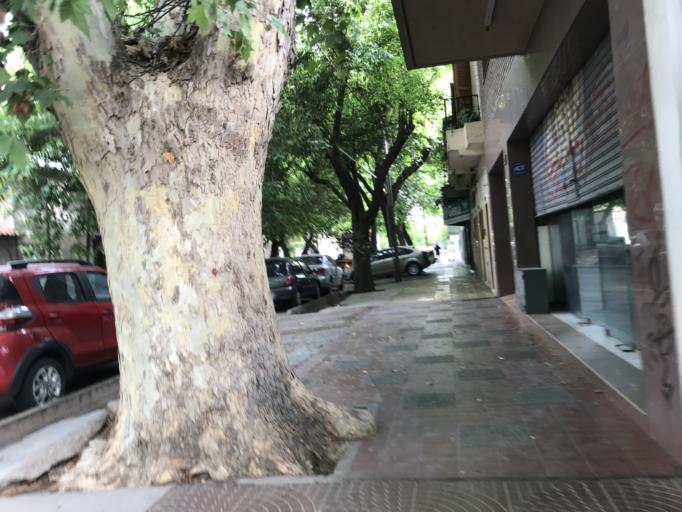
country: AR
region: Mendoza
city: Mendoza
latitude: -32.8802
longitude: -68.8433
